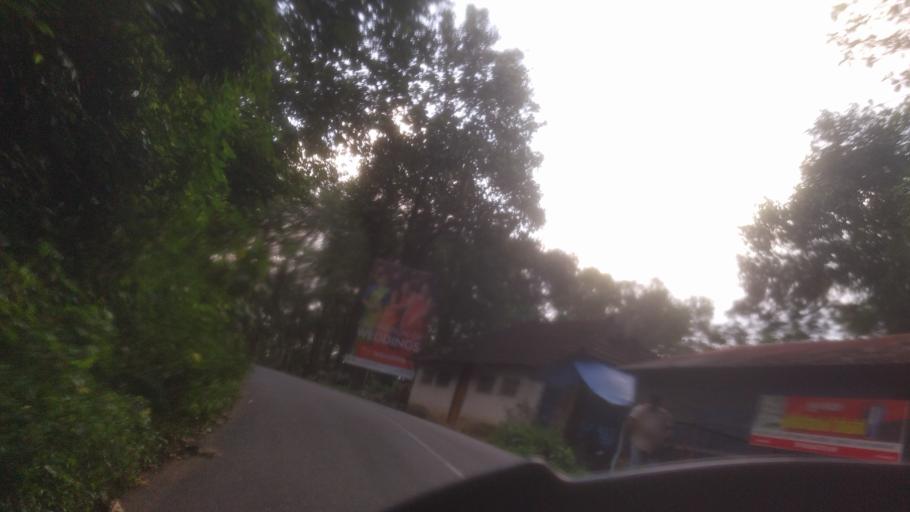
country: IN
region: Kerala
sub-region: Ernakulam
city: Kotamangalam
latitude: 10.0064
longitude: 76.6758
